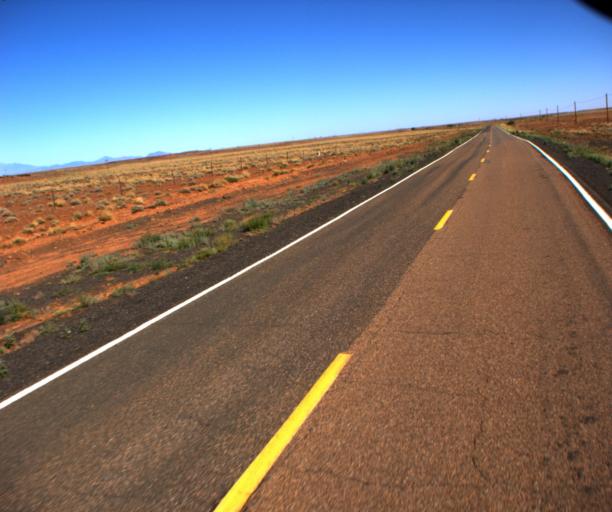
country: US
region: Arizona
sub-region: Coconino County
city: LeChee
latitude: 35.1436
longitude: -110.8927
